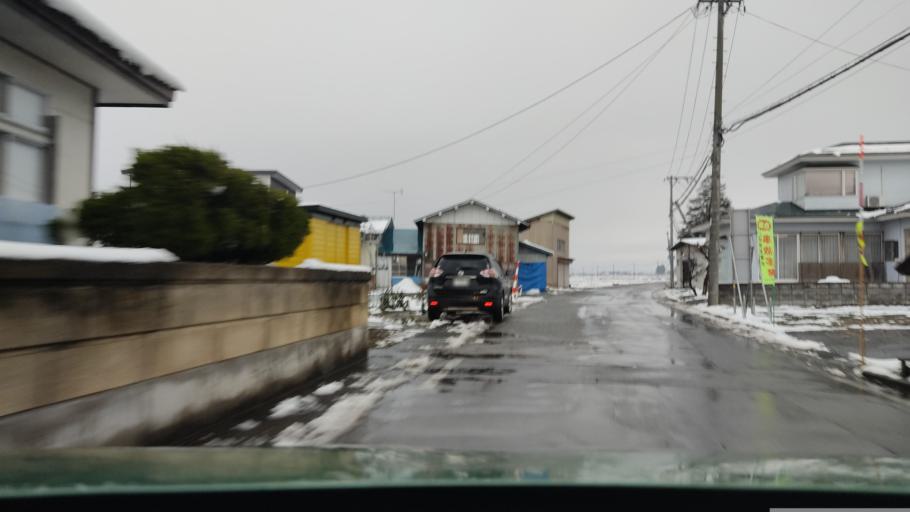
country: JP
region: Akita
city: Omagari
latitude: 39.4718
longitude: 140.5284
